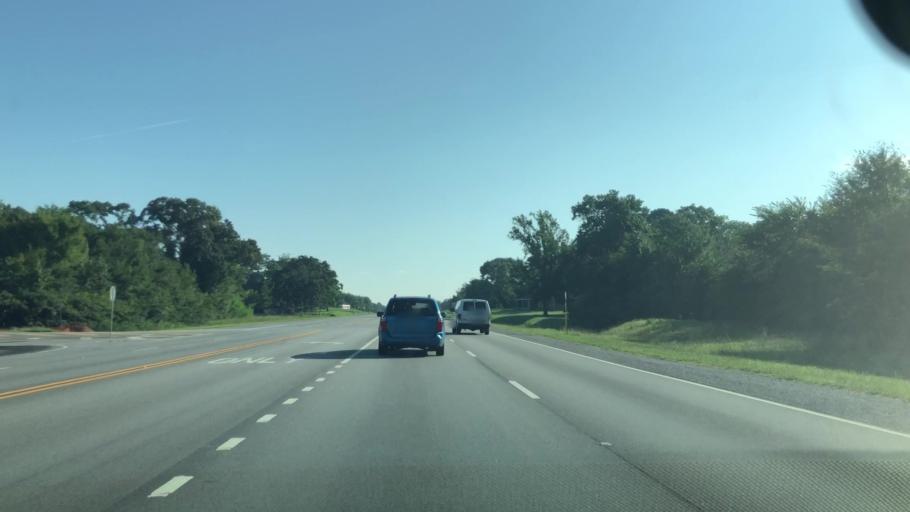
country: US
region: Alabama
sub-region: Calhoun County
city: Bynum
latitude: 33.6204
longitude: -85.9235
